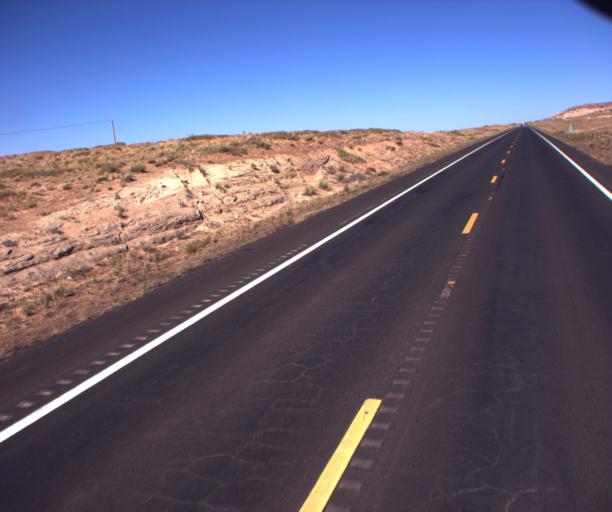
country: US
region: Arizona
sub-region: Coconino County
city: Tuba City
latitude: 36.2230
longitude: -111.0387
